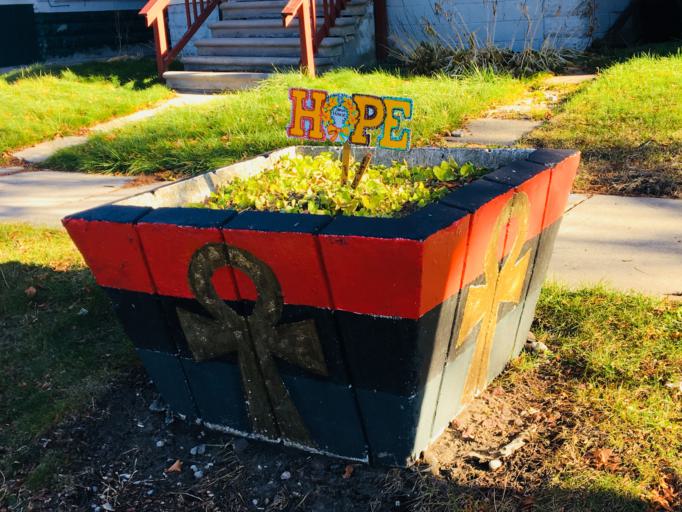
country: US
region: Michigan
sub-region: Wayne County
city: Highland Park
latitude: 42.3609
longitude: -83.0919
